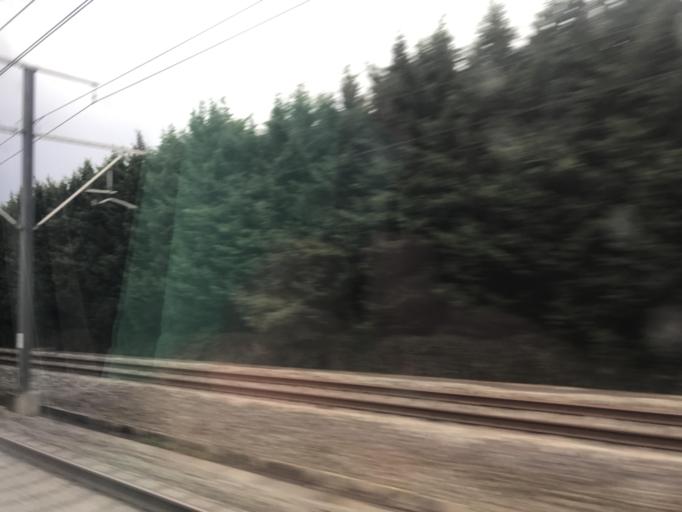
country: BE
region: Flanders
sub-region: Provincie Vlaams-Brabant
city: Bertem
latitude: 50.8975
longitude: 4.5965
